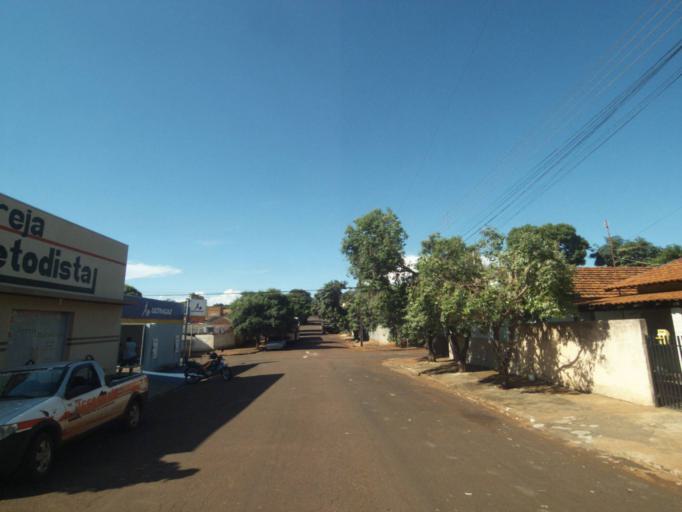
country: BR
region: Parana
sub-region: Sertanopolis
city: Sertanopolis
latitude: -23.0365
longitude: -50.8142
